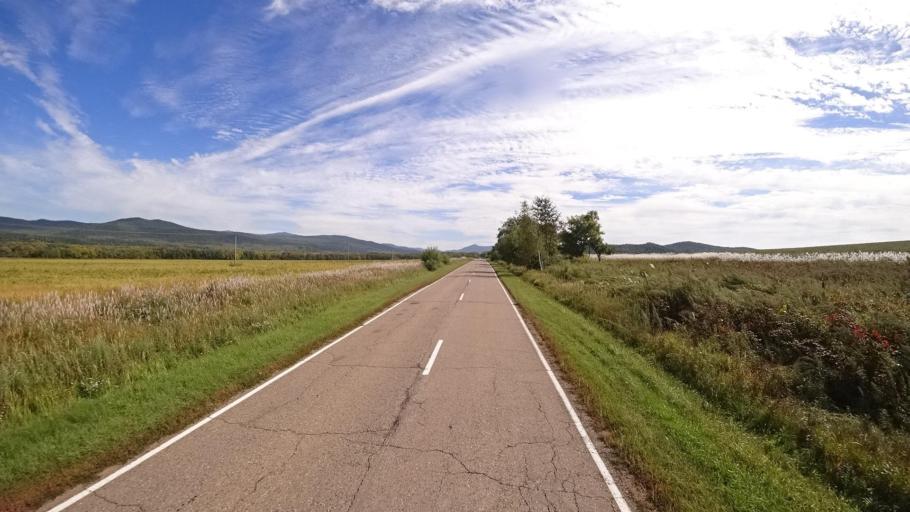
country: RU
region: Primorskiy
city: Yakovlevka
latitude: 44.4171
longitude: 133.5824
